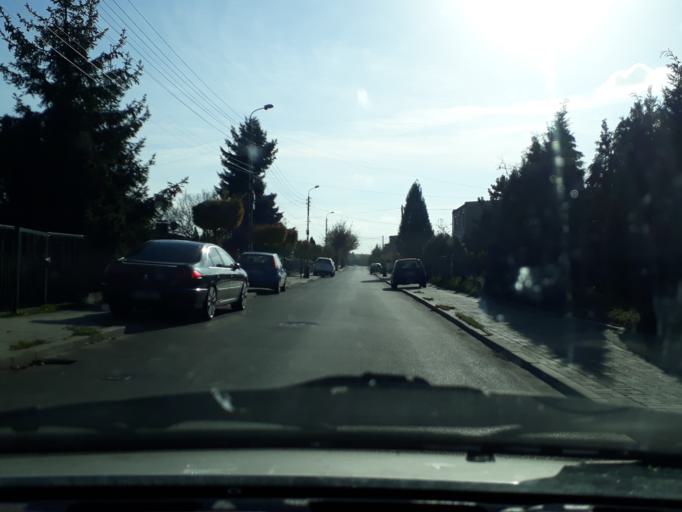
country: PL
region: Silesian Voivodeship
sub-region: Powiat tarnogorski
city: Tarnowskie Gory
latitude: 50.4334
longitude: 18.8442
